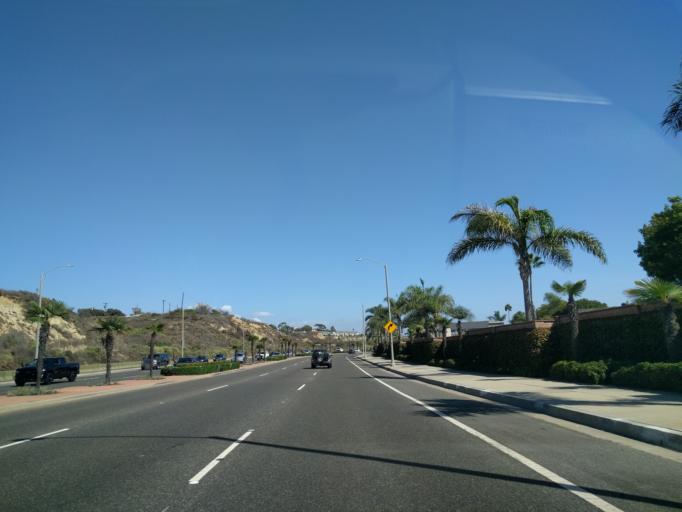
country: US
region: California
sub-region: Orange County
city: Newport Beach
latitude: 33.6251
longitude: -117.9455
